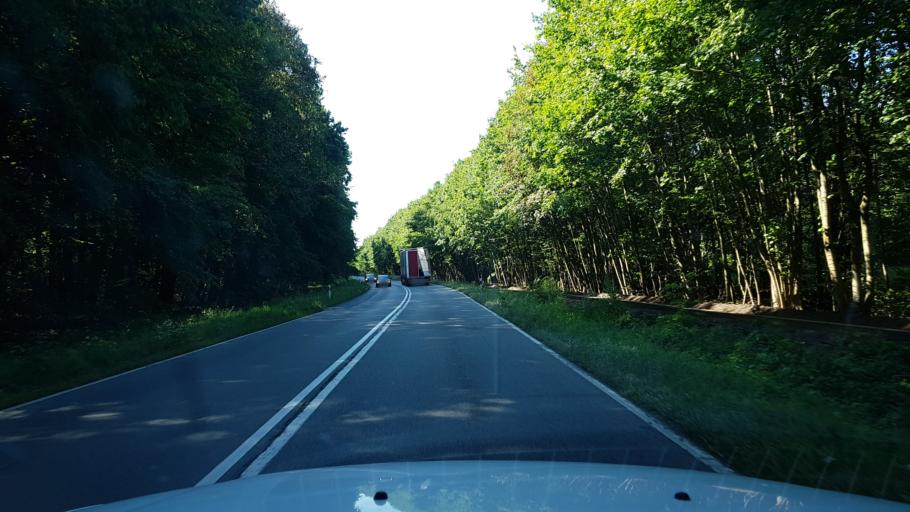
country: PL
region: West Pomeranian Voivodeship
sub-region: Powiat gryfinski
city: Stare Czarnowo
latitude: 53.3290
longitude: 14.7817
